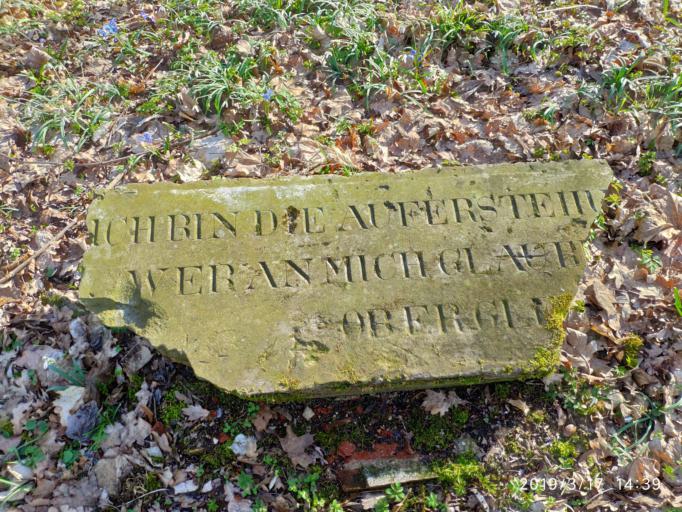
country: PL
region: Lubusz
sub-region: Powiat zielonogorski
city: Zabor
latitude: 51.9498
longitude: 15.7087
